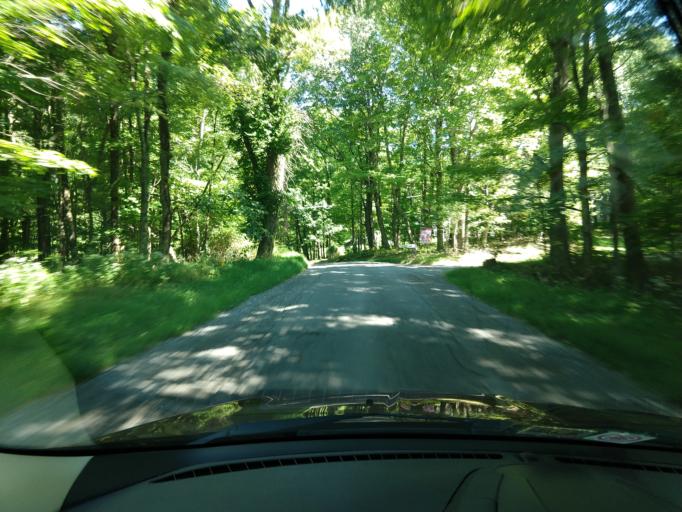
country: US
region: West Virginia
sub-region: Nicholas County
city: Craigsville
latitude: 38.2465
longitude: -80.7052
